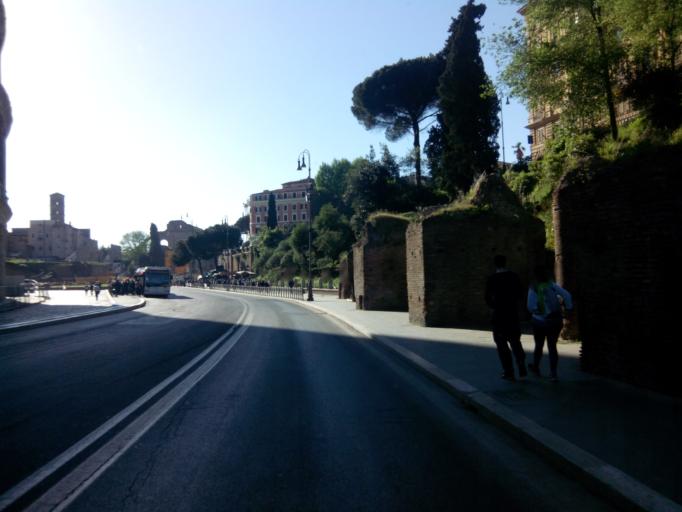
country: IT
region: Latium
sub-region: Citta metropolitana di Roma Capitale
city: Rome
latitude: 41.8908
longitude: 12.4935
